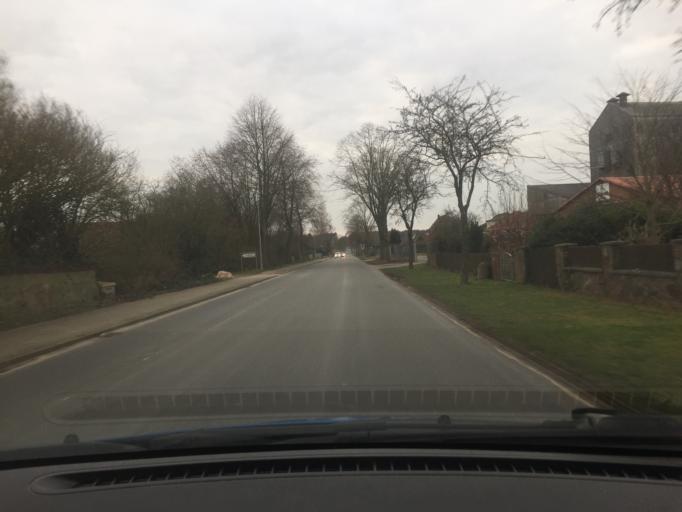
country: DE
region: Lower Saxony
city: Rosche
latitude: 52.9877
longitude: 10.7491
